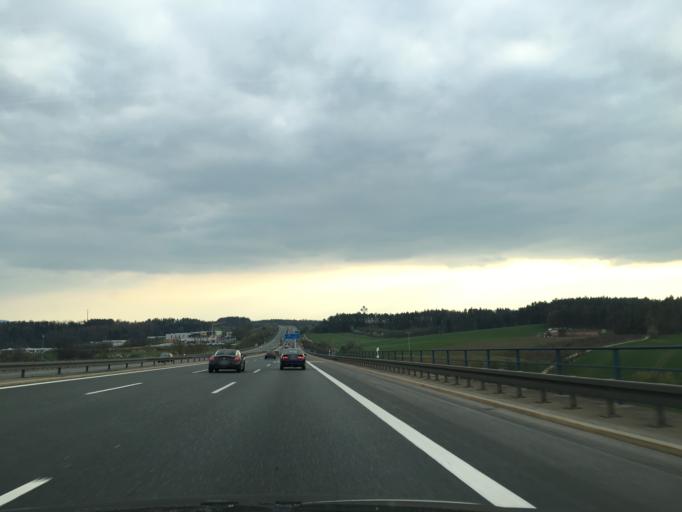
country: DE
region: Bavaria
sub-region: Regierungsbezirk Mittelfranken
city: Schnaittach
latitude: 49.5763
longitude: 11.3406
